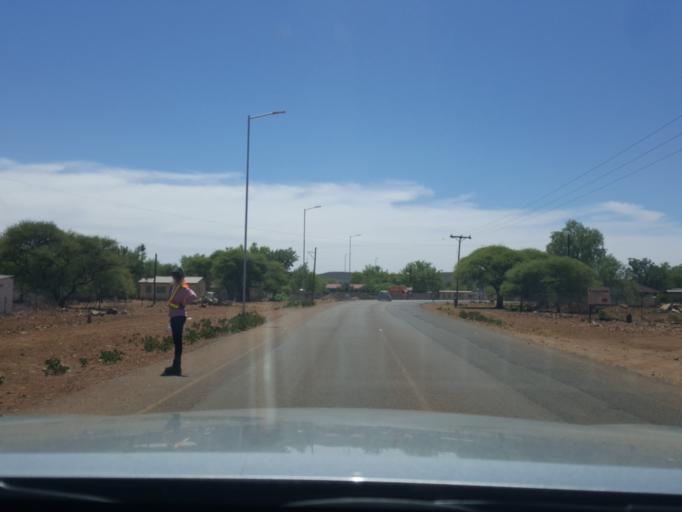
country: BW
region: South East
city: Ramotswa
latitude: -24.8683
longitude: 25.8751
